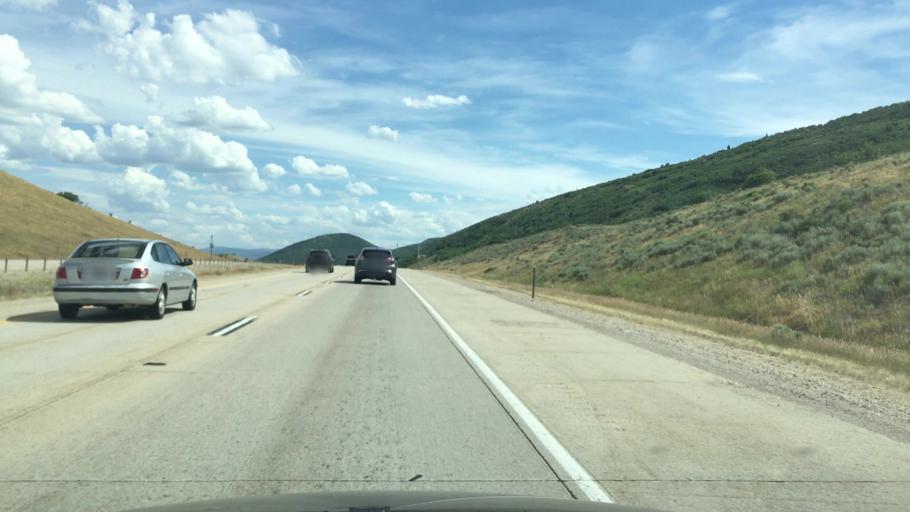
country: US
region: Utah
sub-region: Summit County
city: Park City
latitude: 40.6565
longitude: -111.4576
